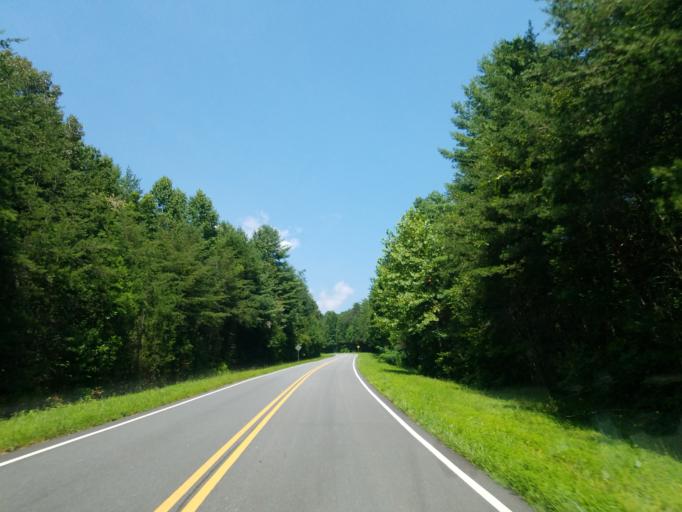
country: US
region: Georgia
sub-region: Lumpkin County
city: Dahlonega
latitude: 34.6217
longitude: -83.8987
